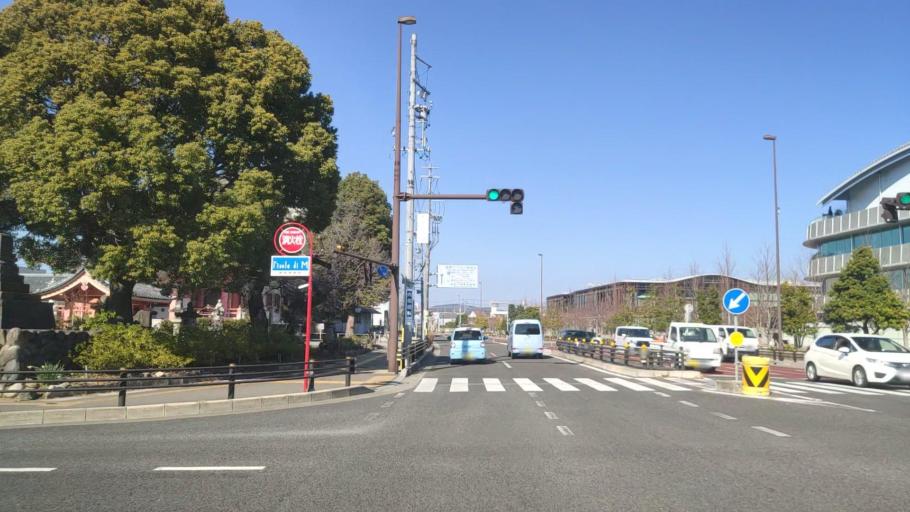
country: JP
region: Gifu
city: Gifu-shi
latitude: 35.4257
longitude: 136.7587
